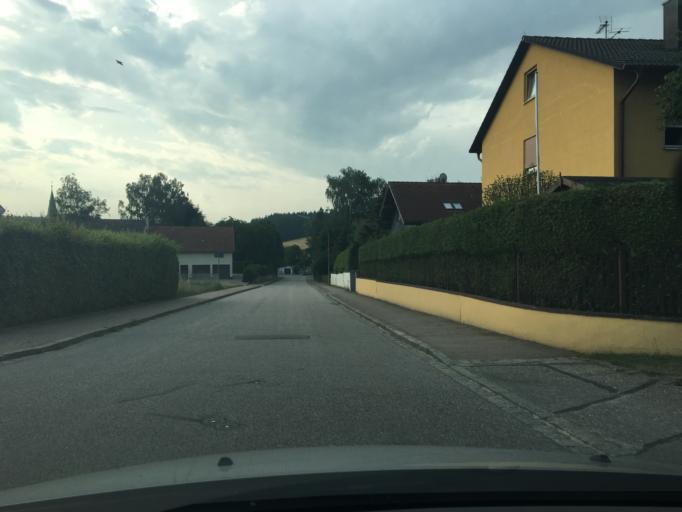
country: DE
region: Bavaria
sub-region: Lower Bavaria
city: Bodenkirchen
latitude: 48.3846
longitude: 12.3844
